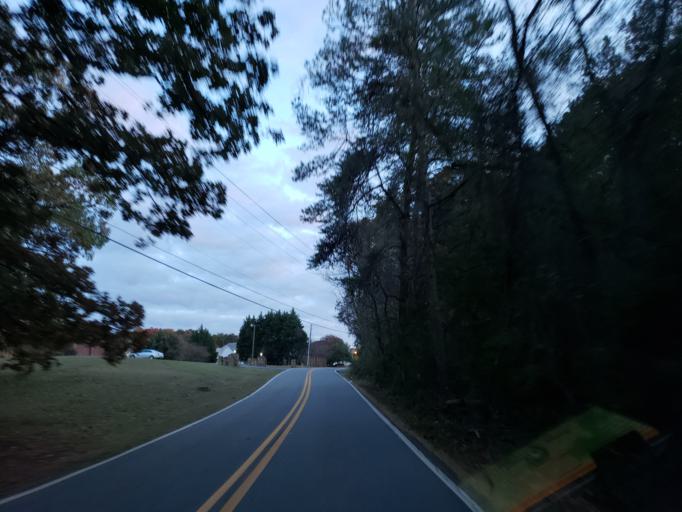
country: US
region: Georgia
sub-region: Bartow County
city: Cartersville
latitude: 34.1959
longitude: -84.7823
